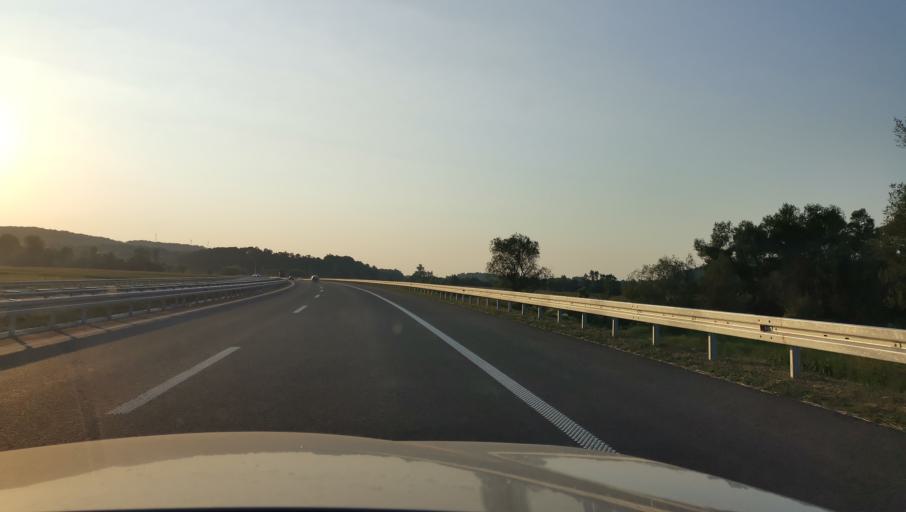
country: RS
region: Central Serbia
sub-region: Kolubarski Okrug
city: Lajkovac
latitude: 44.3332
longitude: 20.2075
